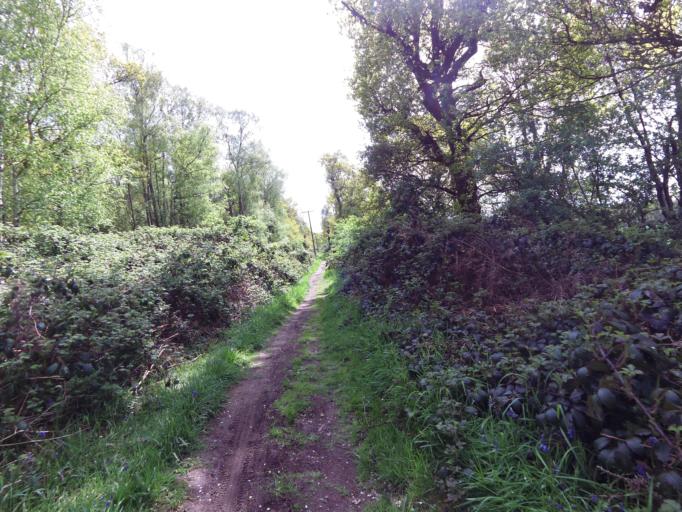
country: GB
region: England
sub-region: Suffolk
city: Ipswich
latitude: 52.0059
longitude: 1.1402
